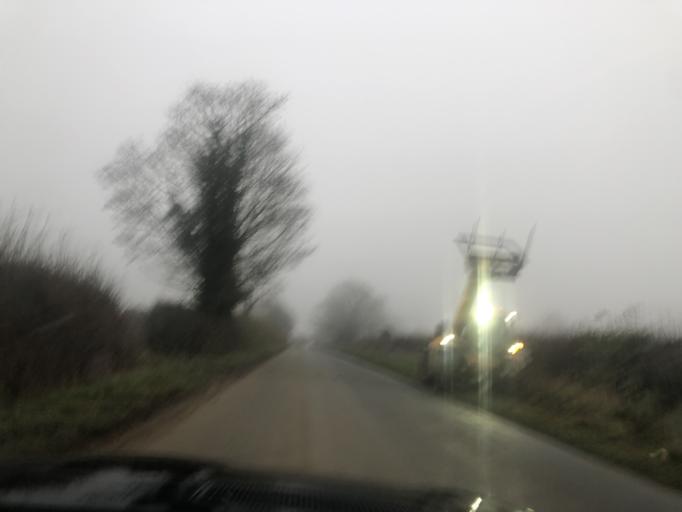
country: GB
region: England
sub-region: Oxfordshire
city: Bicester
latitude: 51.9131
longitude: -1.1725
